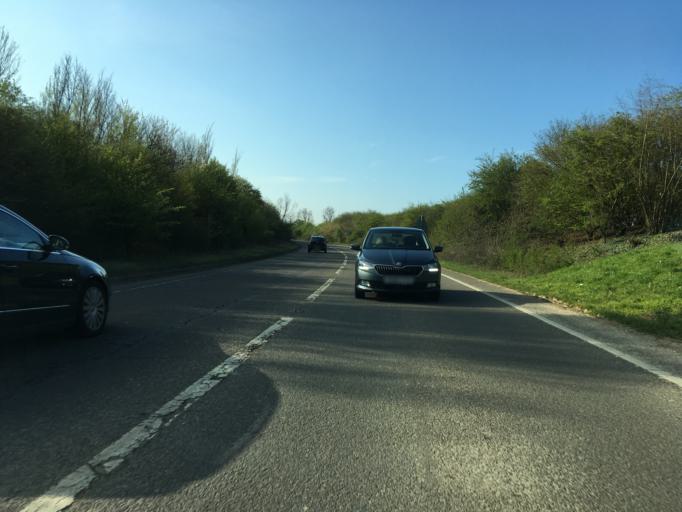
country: GB
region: England
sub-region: Northamptonshire
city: Deanshanger
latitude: 52.0636
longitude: -0.8721
